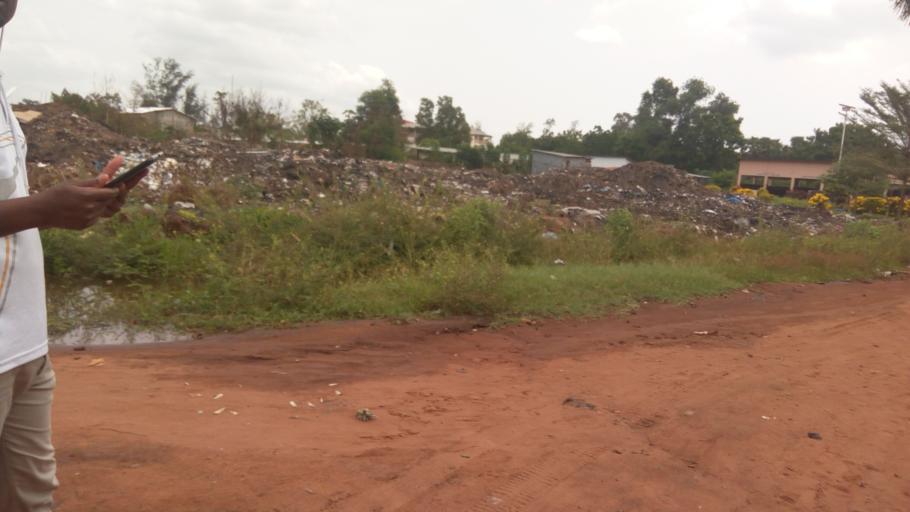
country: BJ
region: Atlantique
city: Abomey-Calavi
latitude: 6.4143
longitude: 2.3380
